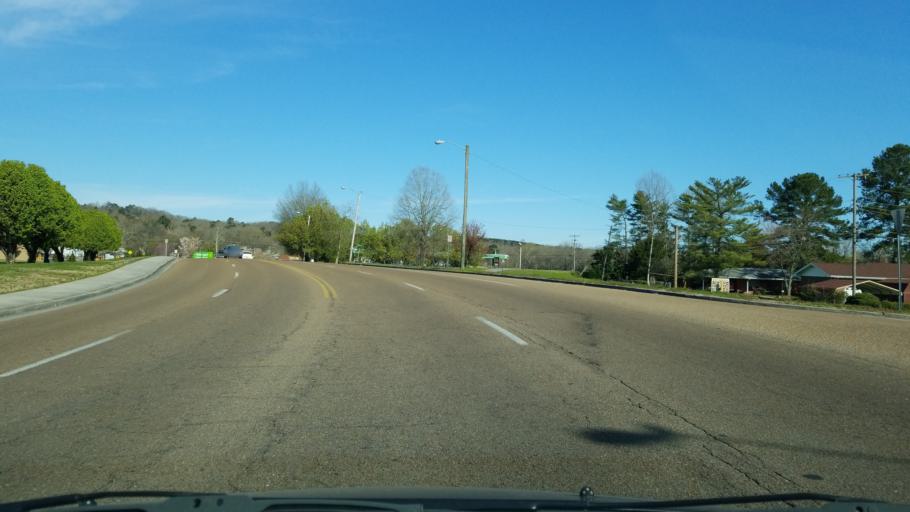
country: US
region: Tennessee
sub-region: Hamilton County
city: East Chattanooga
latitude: 35.0417
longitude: -85.2181
